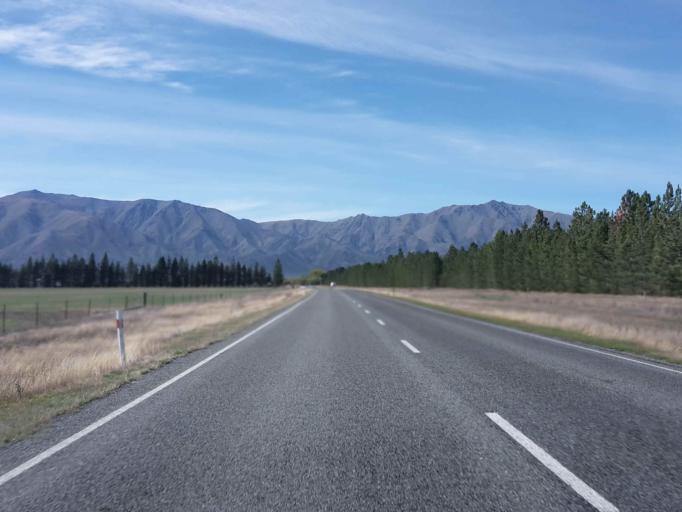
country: NZ
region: Otago
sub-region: Queenstown-Lakes District
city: Wanaka
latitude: -44.4915
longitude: 169.9400
